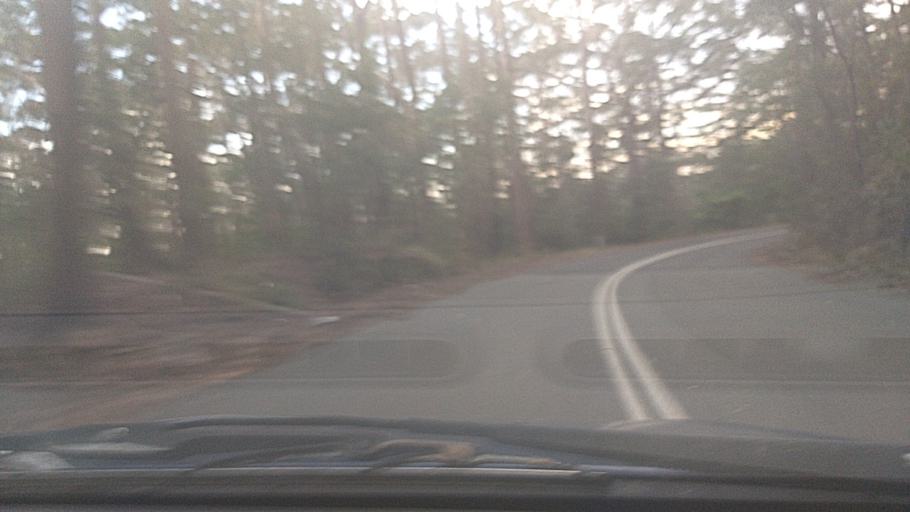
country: AU
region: New South Wales
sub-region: Wollongong
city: Mount Ousley
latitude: -34.3877
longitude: 150.8503
